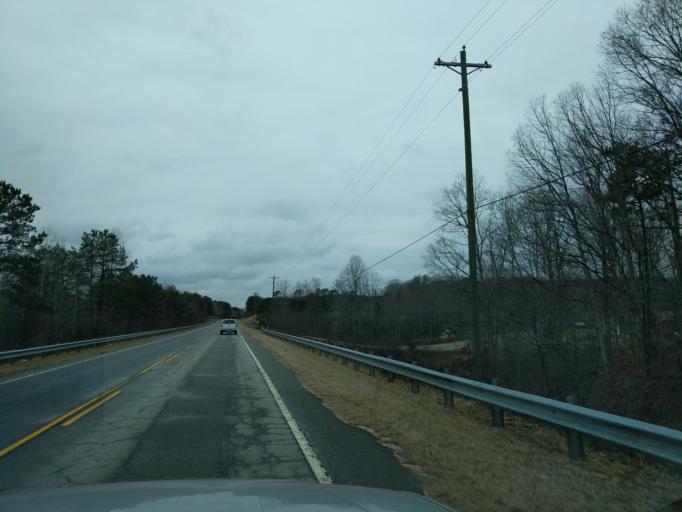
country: US
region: South Carolina
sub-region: Oconee County
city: Walhalla
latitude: 34.9126
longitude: -82.9407
